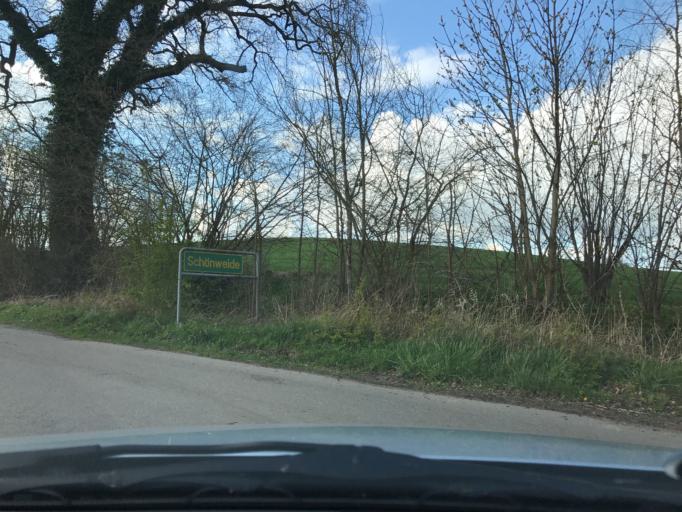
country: DE
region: Schleswig-Holstein
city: Grebin
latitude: 54.2241
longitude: 10.4926
